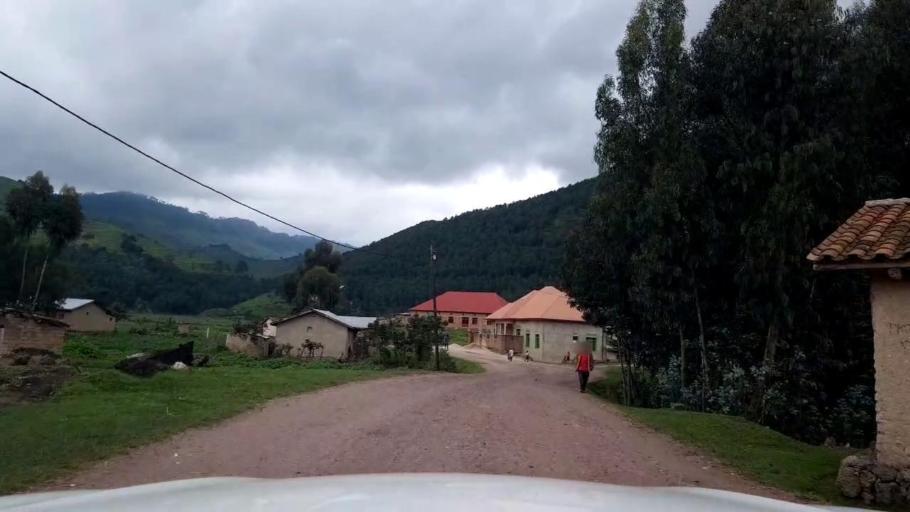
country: RW
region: Western Province
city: Gisenyi
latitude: -1.6424
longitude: 29.4089
